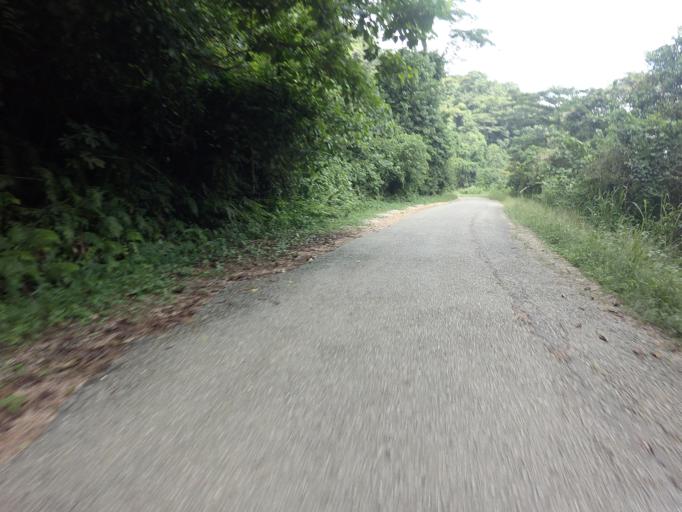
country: GH
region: Volta
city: Kpandu
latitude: 6.8346
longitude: 0.4266
